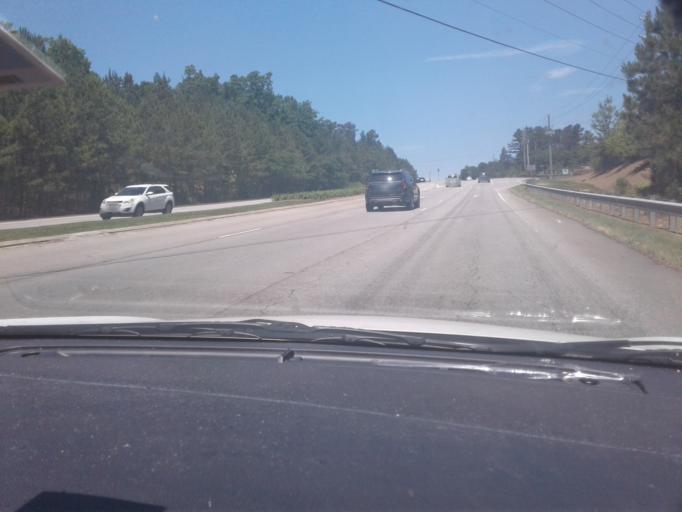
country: US
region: North Carolina
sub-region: Wake County
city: Holly Springs
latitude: 35.6223
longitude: -78.8180
